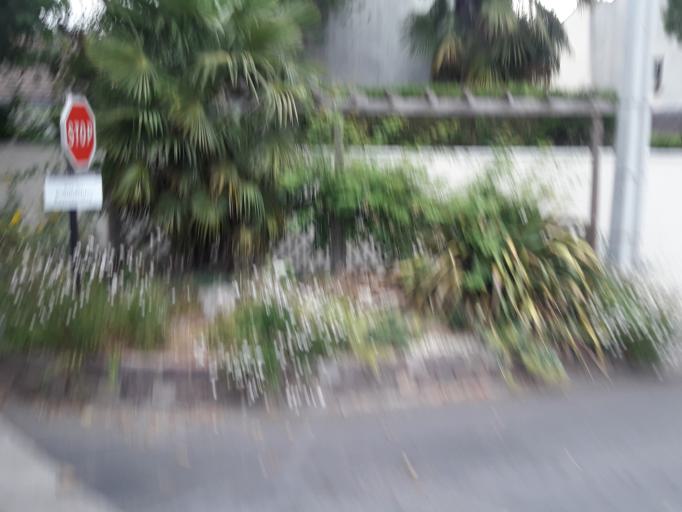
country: FR
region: Ile-de-France
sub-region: Departement de l'Essonne
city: Longjumeau
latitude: 48.6962
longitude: 2.2989
